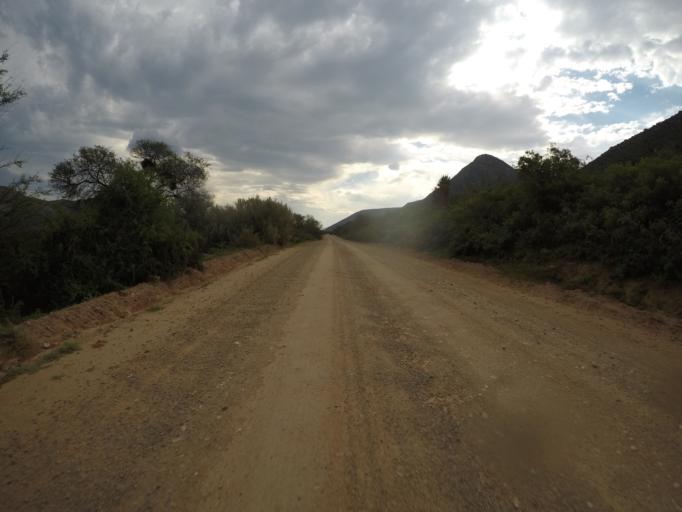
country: ZA
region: Eastern Cape
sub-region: Cacadu District Municipality
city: Kareedouw
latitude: -33.5801
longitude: 24.1530
